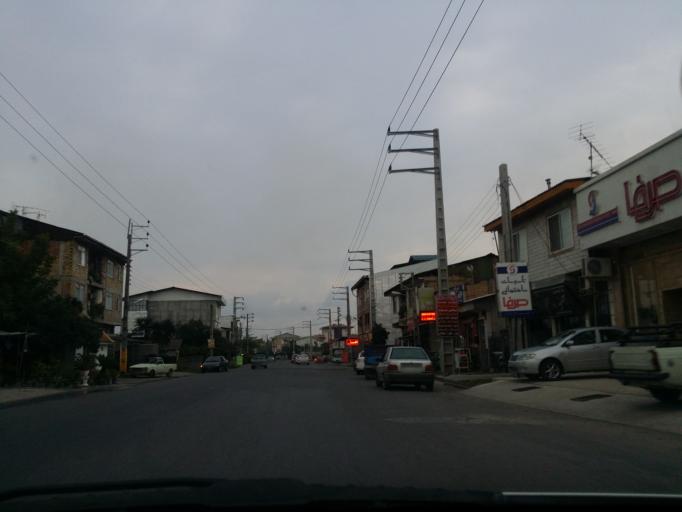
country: IR
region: Mazandaran
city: `Abbasabad
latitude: 36.7117
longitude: 51.1010
